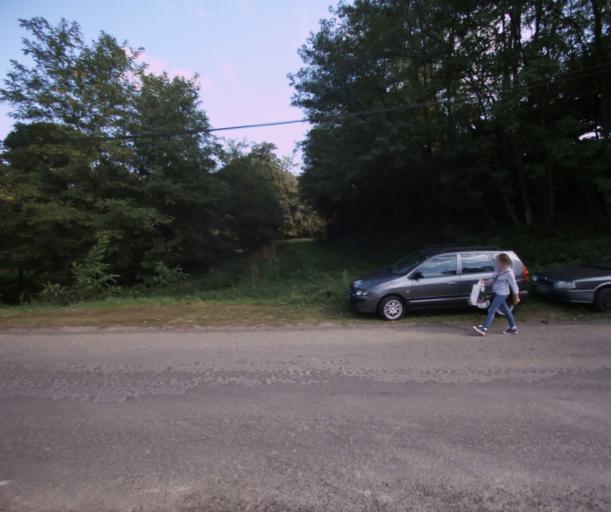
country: FR
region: Midi-Pyrenees
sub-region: Departement du Gers
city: Cazaubon
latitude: 43.9371
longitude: -0.0719
